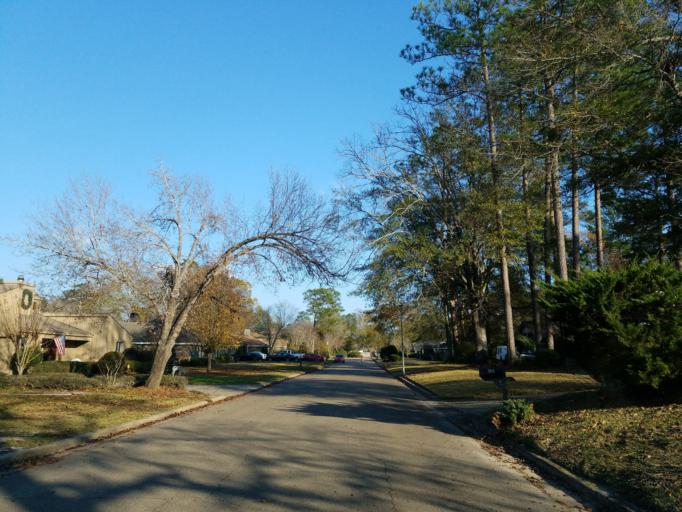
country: US
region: Mississippi
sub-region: Lamar County
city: West Hattiesburg
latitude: 31.3052
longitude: -89.3428
